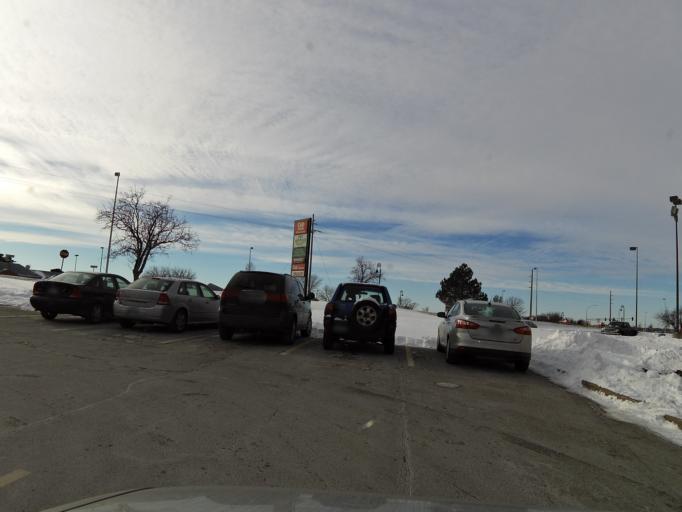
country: US
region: Minnesota
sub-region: Dakota County
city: Burnsville
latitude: 44.7472
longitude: -93.3002
